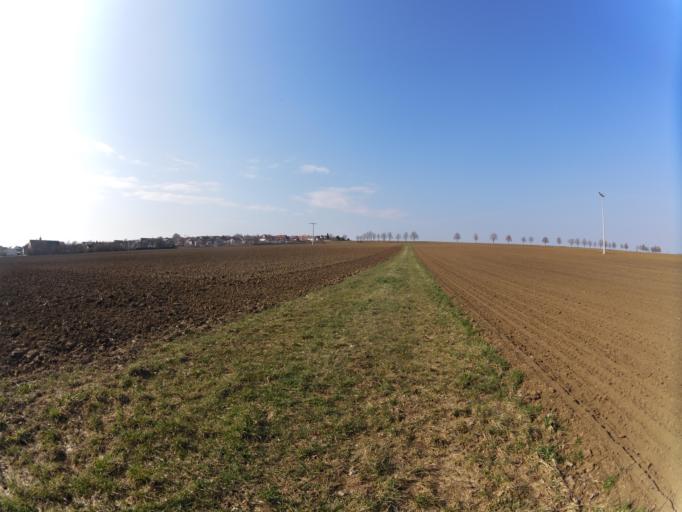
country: DE
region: Bavaria
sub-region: Regierungsbezirk Unterfranken
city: Sulzdorf
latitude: 49.6501
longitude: 9.9122
